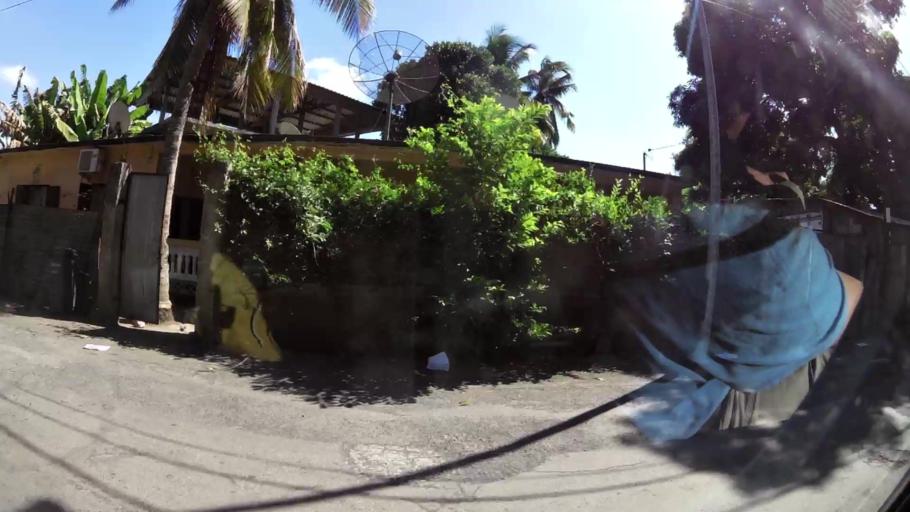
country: YT
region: Pamandzi
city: Pamandzi
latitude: -12.7942
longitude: 45.2795
